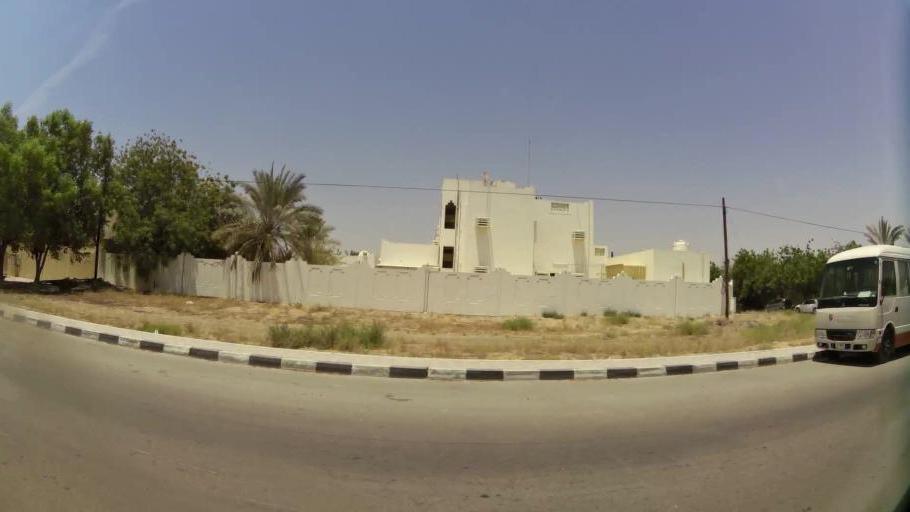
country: AE
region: Ajman
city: Ajman
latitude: 25.4193
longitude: 55.5005
